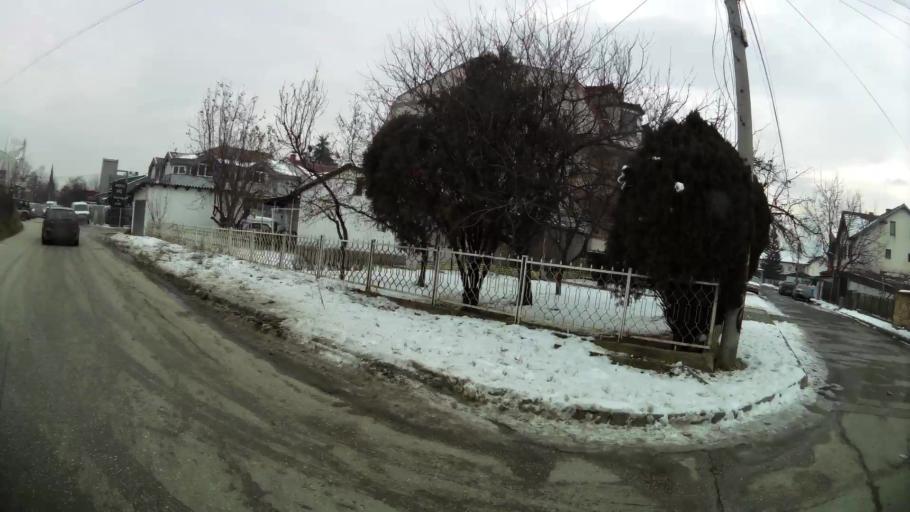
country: MK
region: Butel
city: Butel
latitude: 42.0306
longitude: 21.4435
